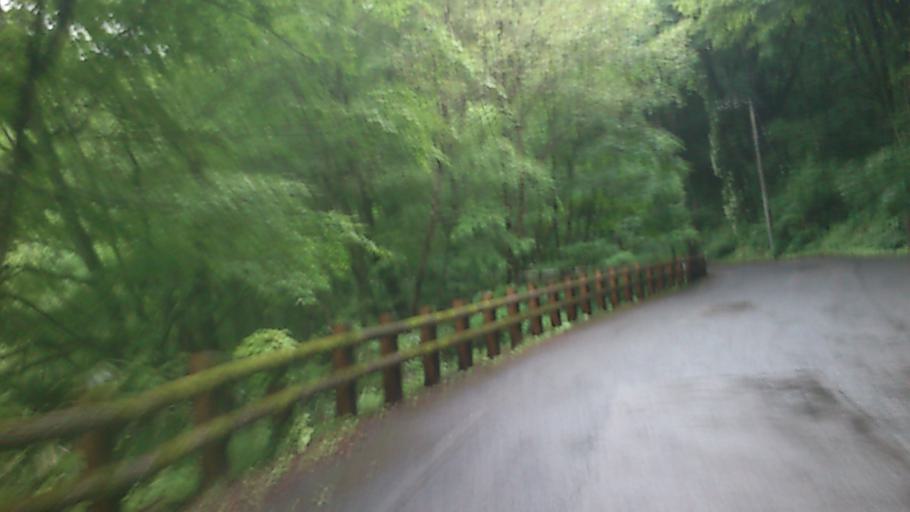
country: JP
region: Akita
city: Noshiromachi
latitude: 40.5652
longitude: 139.9795
